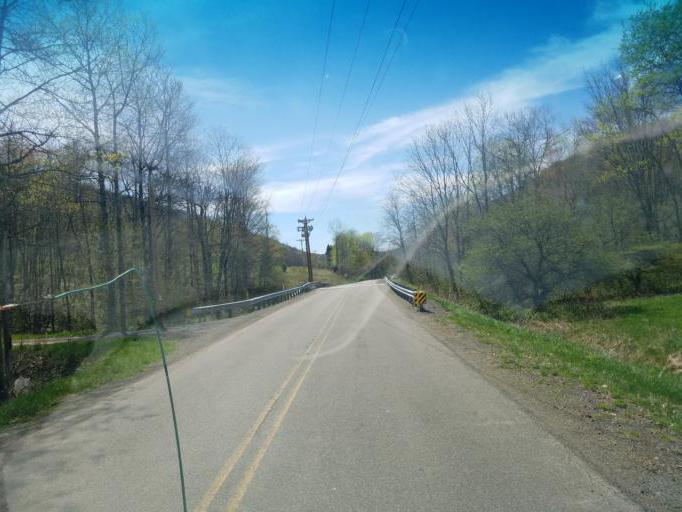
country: US
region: Pennsylvania
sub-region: Potter County
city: Galeton
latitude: 41.8745
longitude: -77.7275
